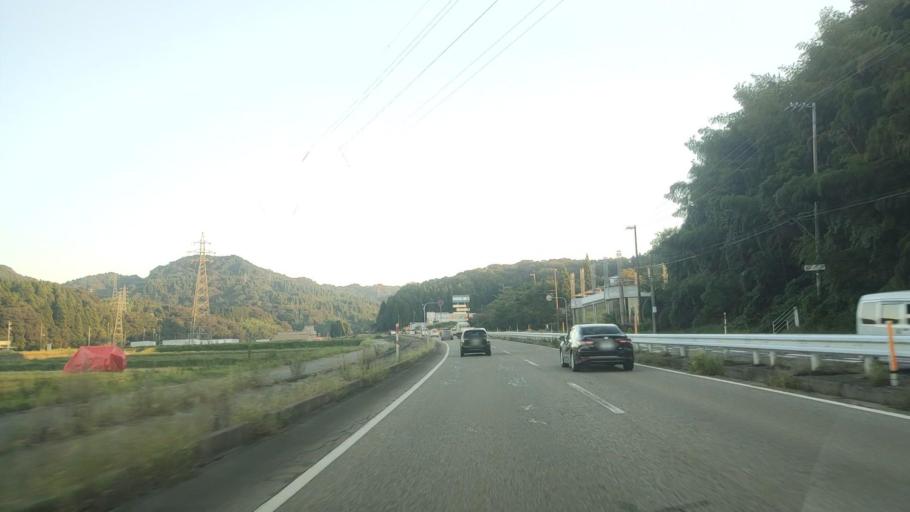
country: JP
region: Toyama
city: Himi
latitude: 36.8087
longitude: 136.9974
